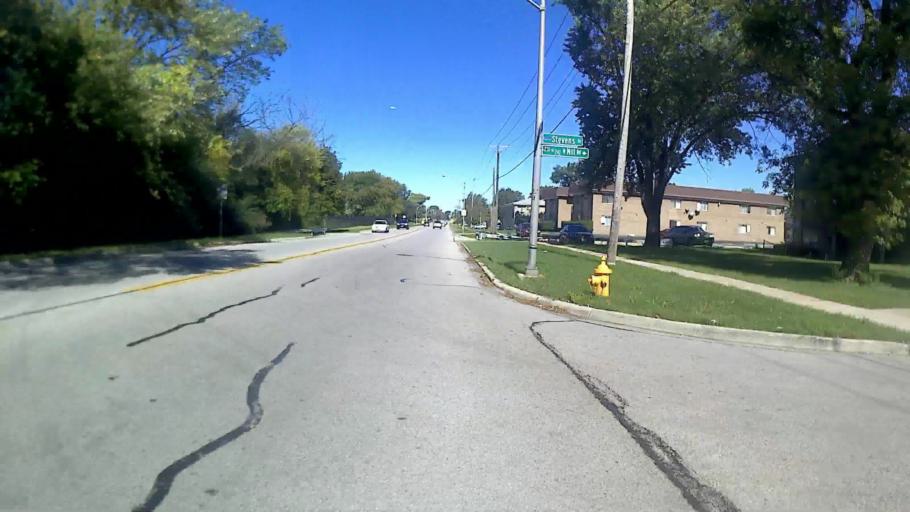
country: US
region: Illinois
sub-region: DuPage County
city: Addison
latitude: 41.9334
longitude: -88.0034
